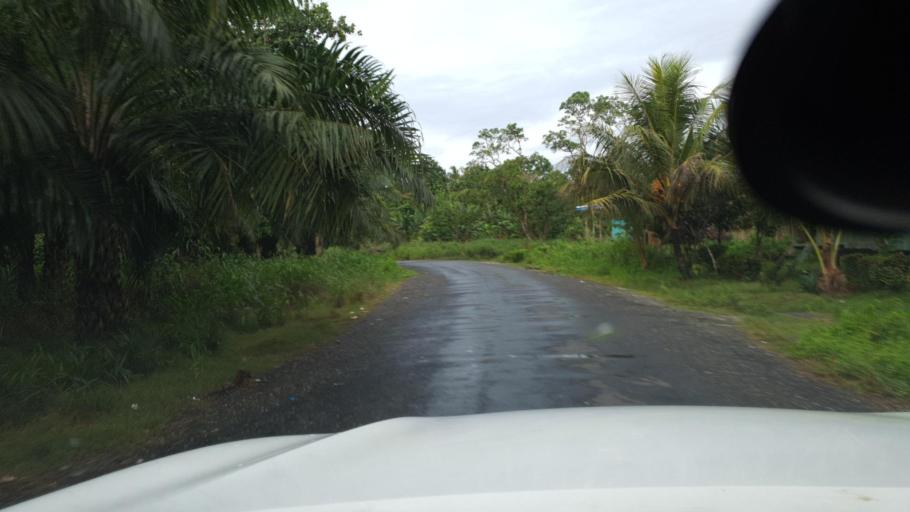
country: SB
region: Guadalcanal
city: Honiara
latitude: -9.4796
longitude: 160.3591
